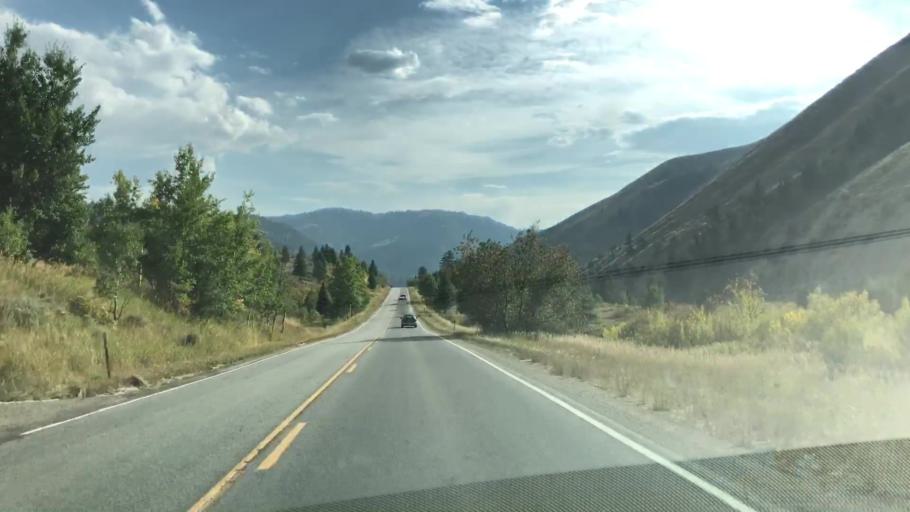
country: US
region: Wyoming
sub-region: Teton County
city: Hoback
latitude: 43.3369
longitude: -110.7249
